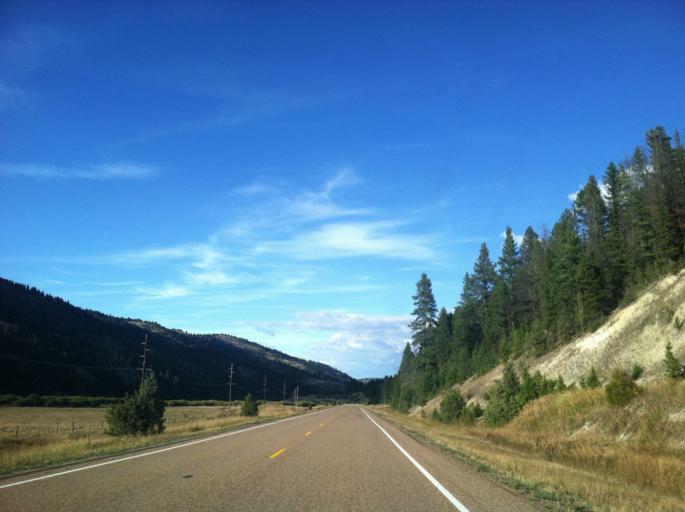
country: US
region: Montana
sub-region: Granite County
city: Philipsburg
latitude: 46.4076
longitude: -113.2925
